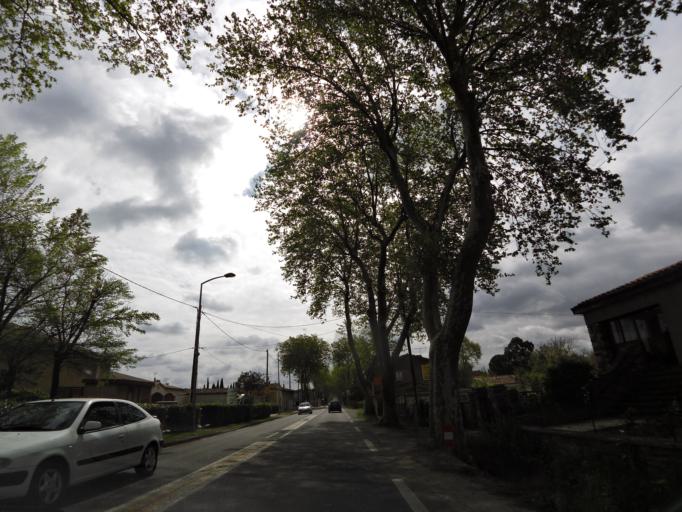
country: FR
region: Languedoc-Roussillon
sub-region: Departement de l'Aude
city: Castelnaudary
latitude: 43.3144
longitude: 1.9633
